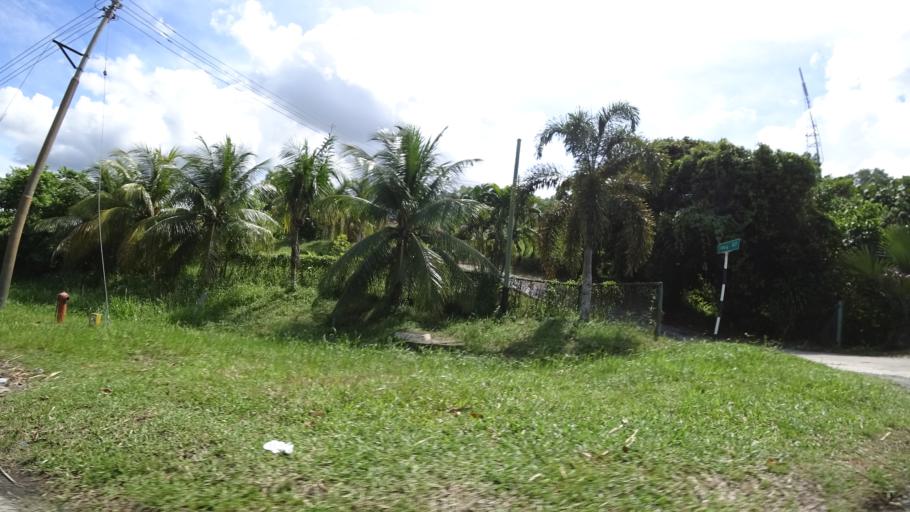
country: BN
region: Brunei and Muara
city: Bandar Seri Begawan
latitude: 4.8800
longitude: 114.9631
